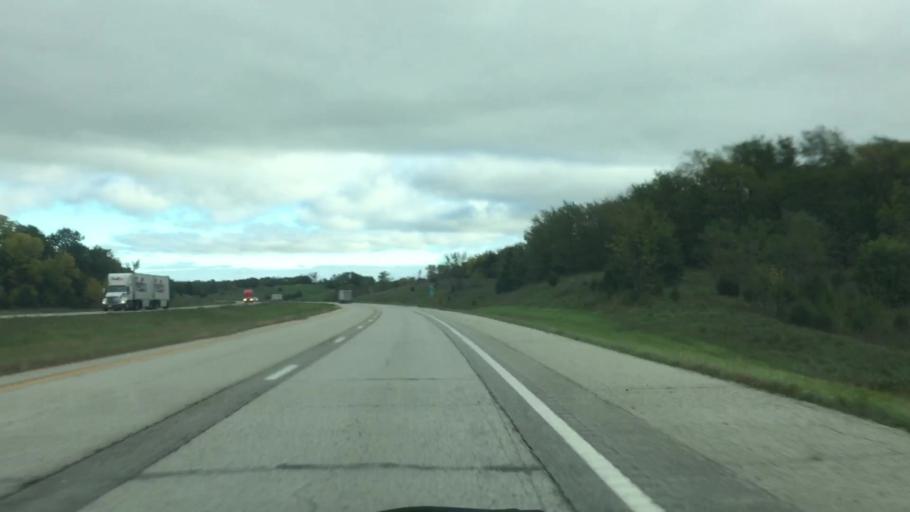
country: US
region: Missouri
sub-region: Harrison County
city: Bethany
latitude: 40.1772
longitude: -94.0165
